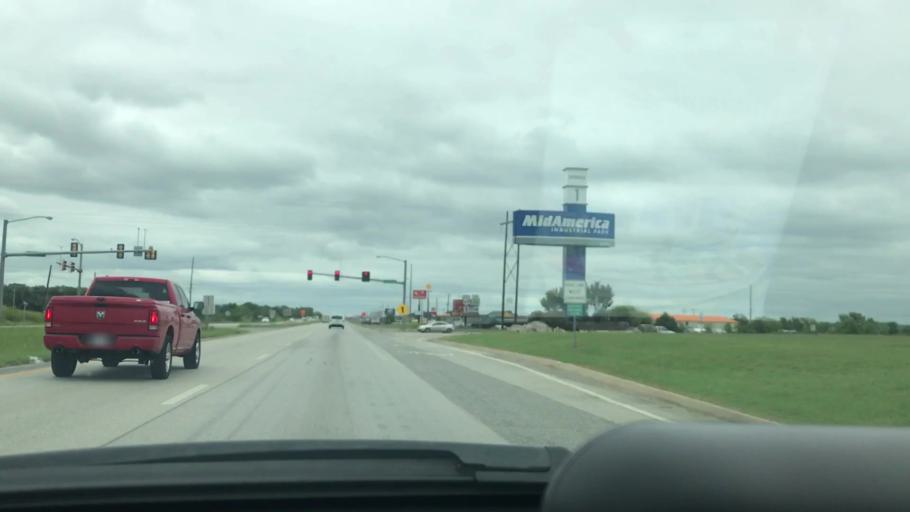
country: US
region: Oklahoma
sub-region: Mayes County
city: Chouteau
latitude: 36.2468
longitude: -95.3363
